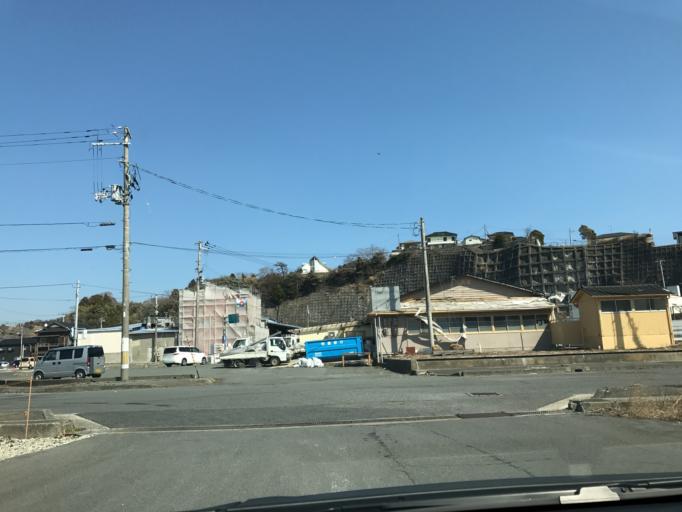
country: JP
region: Fukushima
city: Iwaki
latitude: 36.9430
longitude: 140.9136
